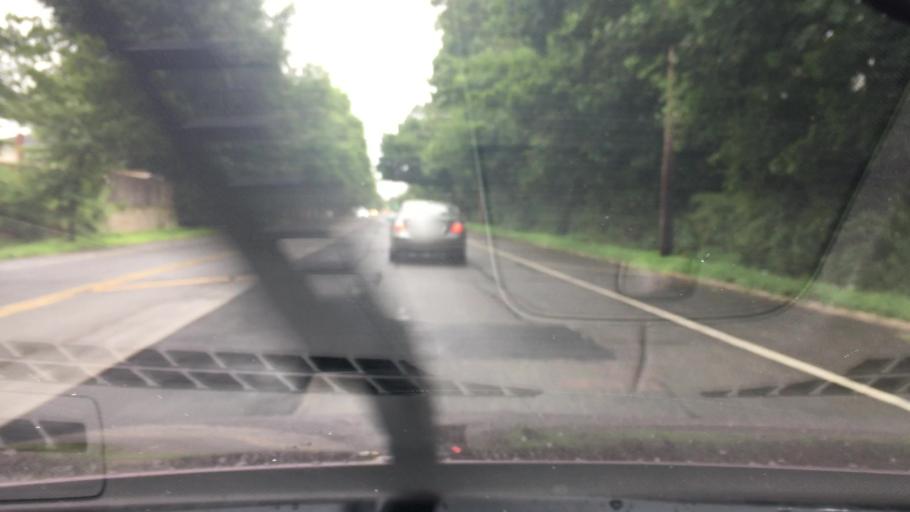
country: US
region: New York
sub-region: Nassau County
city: Old Bethpage
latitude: 40.7673
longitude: -73.4568
